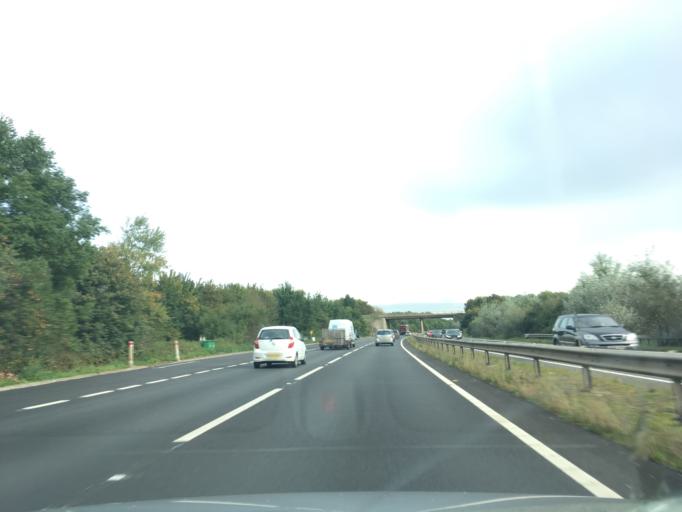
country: GB
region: England
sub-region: Oxfordshire
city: Kidlington
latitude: 51.8220
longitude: -1.2634
